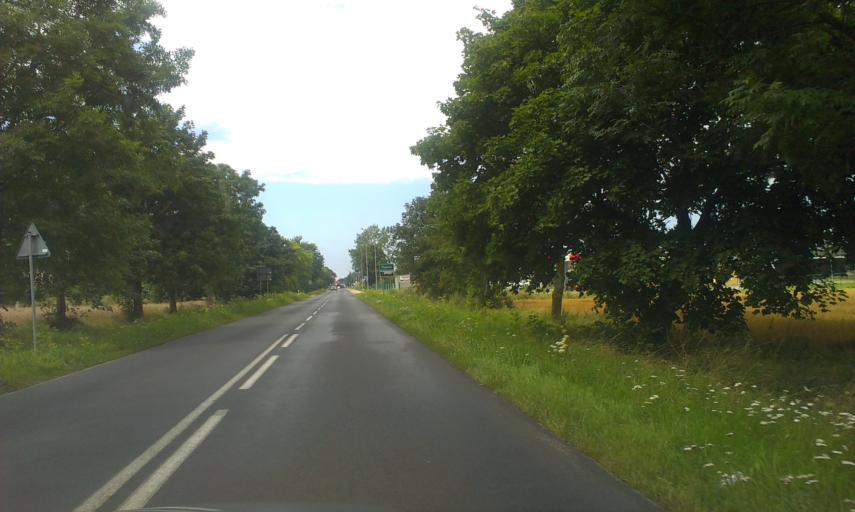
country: PL
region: West Pomeranian Voivodeship
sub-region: Powiat kolobrzeski
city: Dygowo
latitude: 54.1263
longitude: 15.7289
